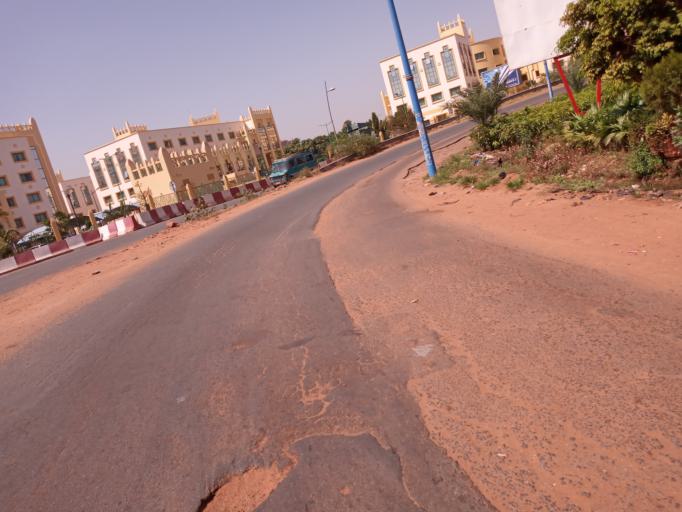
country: ML
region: Bamako
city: Bamako
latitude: 12.6277
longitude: -8.0087
